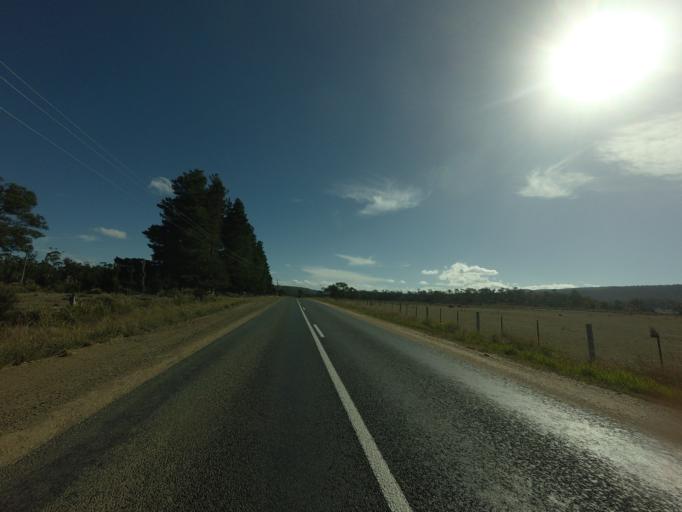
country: AU
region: Tasmania
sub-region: Break O'Day
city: St Helens
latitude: -41.9454
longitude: 148.2072
